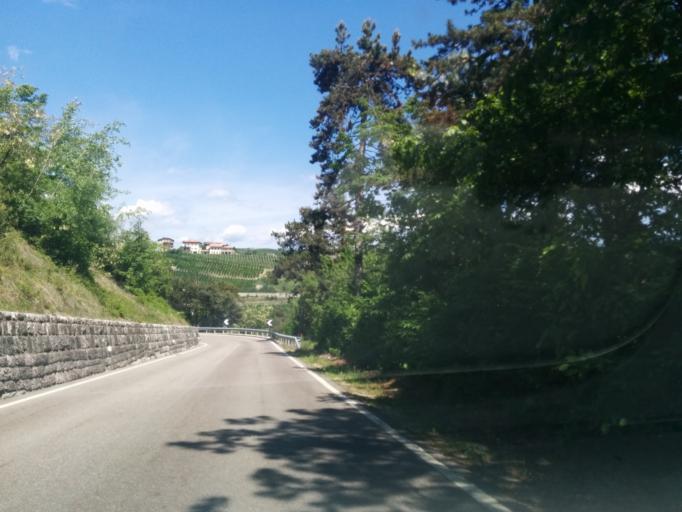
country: IT
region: Trentino-Alto Adige
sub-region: Provincia di Trento
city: Terres
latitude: 46.3146
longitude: 11.0201
